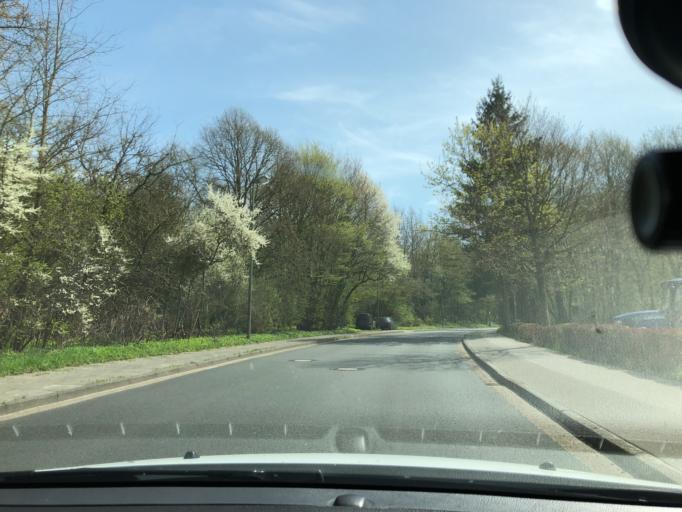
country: DE
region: Schleswig-Holstein
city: Flensburg
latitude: 54.7745
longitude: 9.4462
